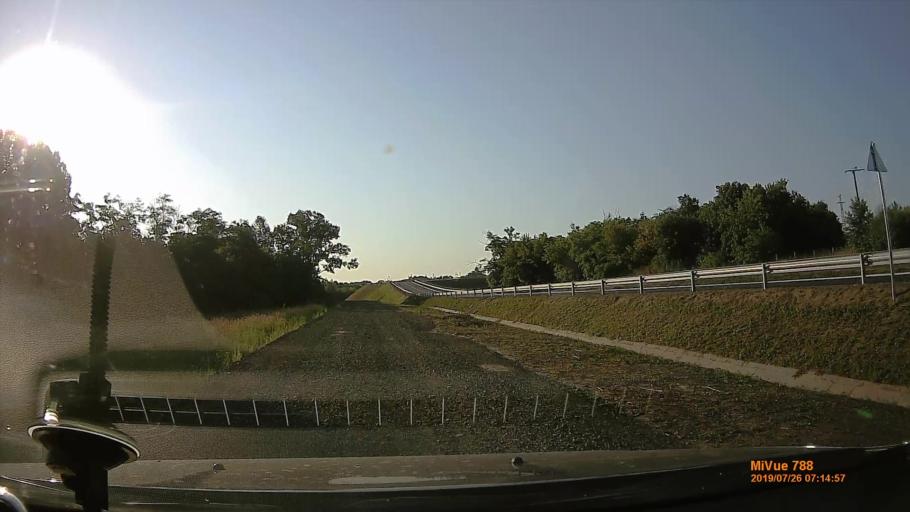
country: HU
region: Pest
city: Mogyorod
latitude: 47.5950
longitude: 19.2259
